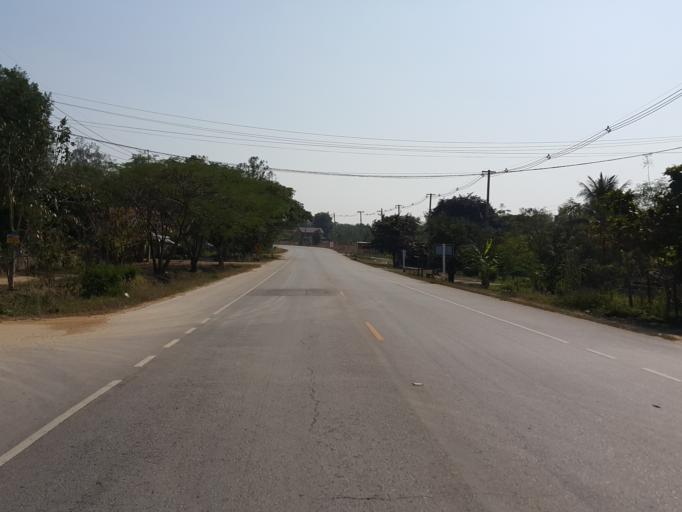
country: TH
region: Lampang
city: Chae Hom
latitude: 18.7413
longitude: 99.5772
